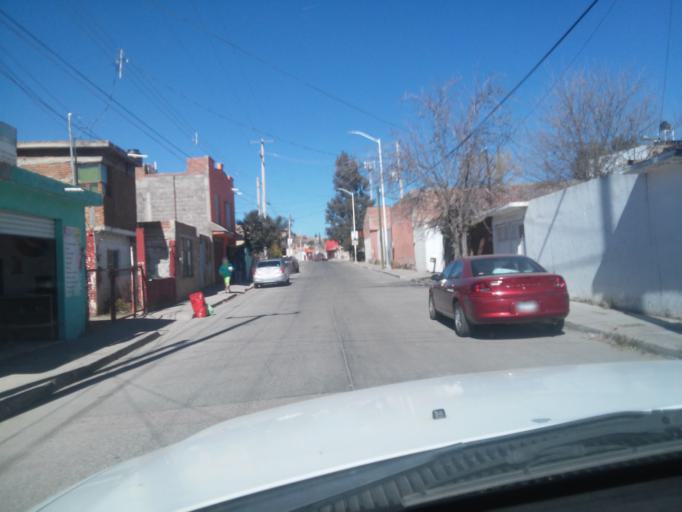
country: MX
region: Durango
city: Victoria de Durango
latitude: 24.0305
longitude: -104.6892
